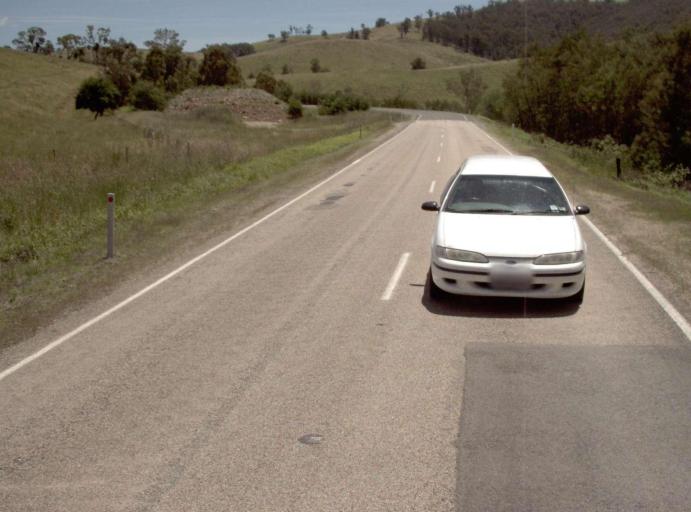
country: AU
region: Victoria
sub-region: East Gippsland
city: Bairnsdale
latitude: -37.5003
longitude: 147.8419
